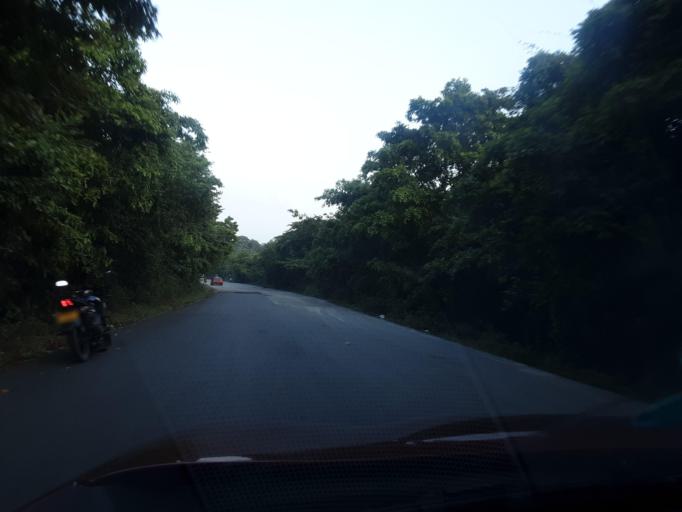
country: LK
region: Central
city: Dambulla
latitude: 7.8104
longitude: 80.7690
